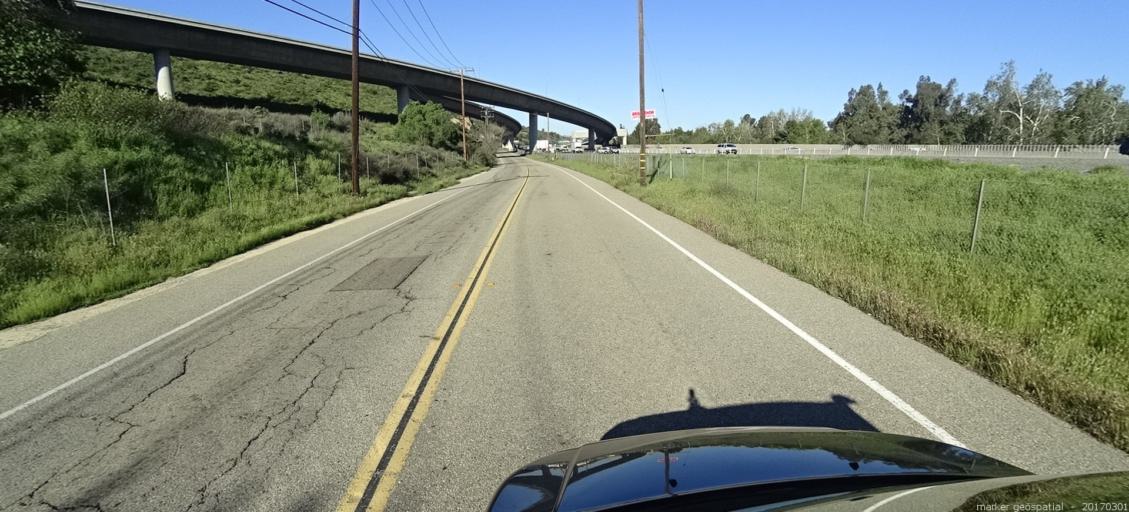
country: US
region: California
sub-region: Orange County
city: Yorba Linda
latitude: 33.8660
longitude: -117.7171
